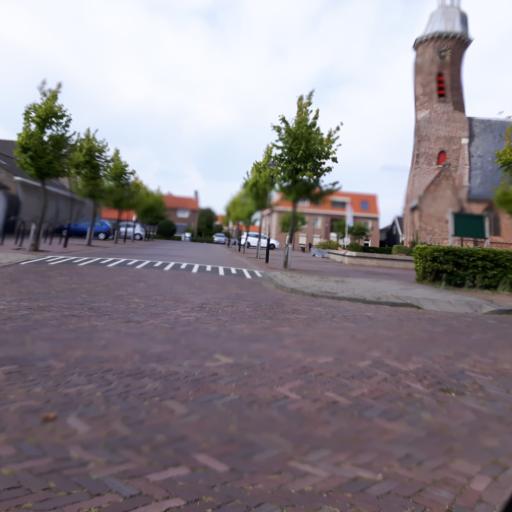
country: NL
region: Zeeland
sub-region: Gemeente Goes
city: Goes
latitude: 51.4572
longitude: 3.8988
